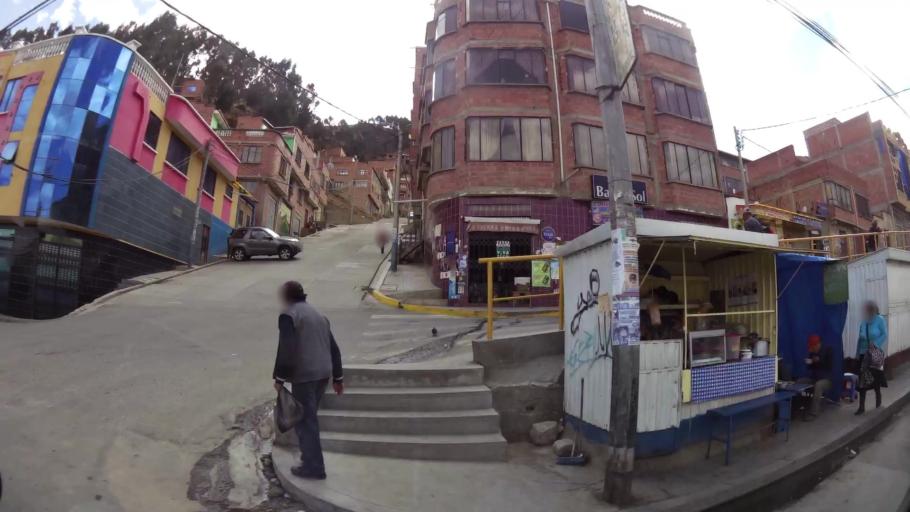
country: BO
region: La Paz
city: La Paz
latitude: -16.4658
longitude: -68.1191
